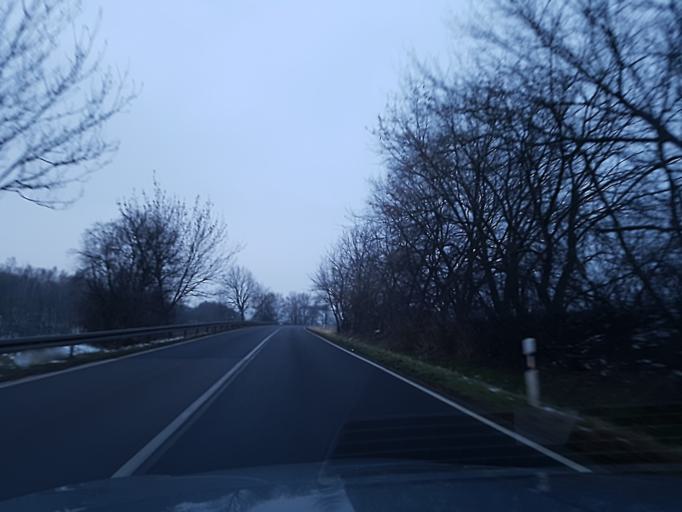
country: DE
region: Saxony
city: Ostrau
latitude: 51.1870
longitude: 13.1449
